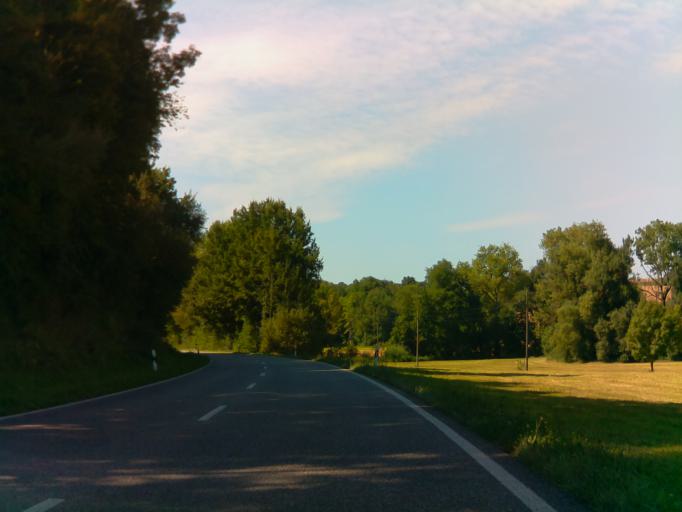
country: DE
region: Baden-Wuerttemberg
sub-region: Karlsruhe Region
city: Oberderdingen
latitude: 49.0909
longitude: 8.7655
